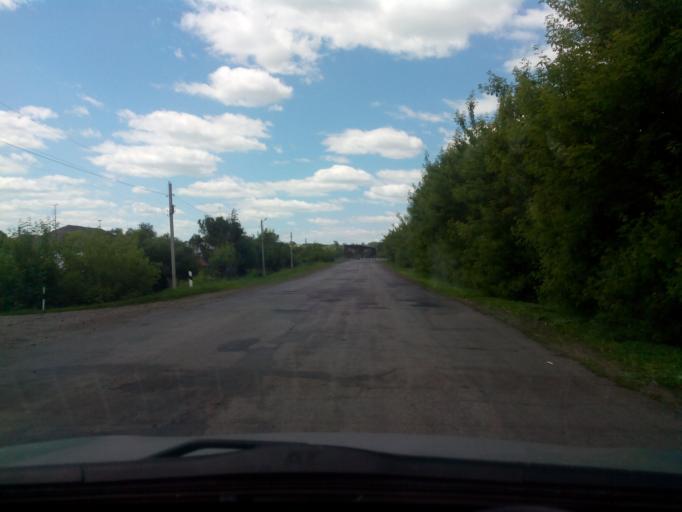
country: RU
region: Voronezj
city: Ternovka
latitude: 51.6237
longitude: 41.7751
